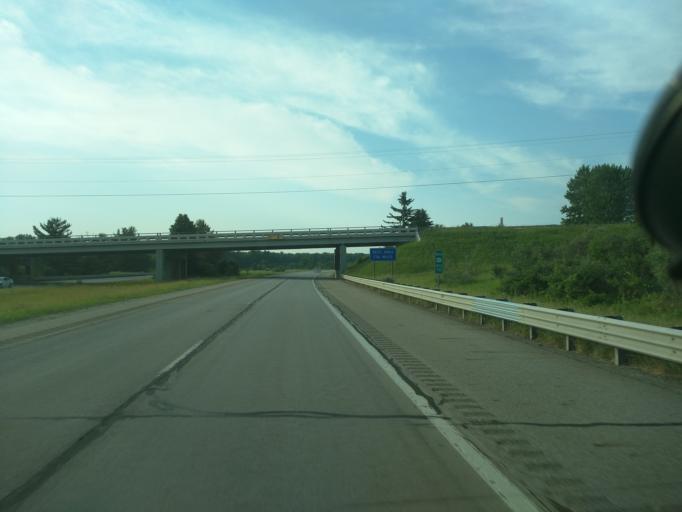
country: US
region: Michigan
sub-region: Ingham County
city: Holt
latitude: 42.6394
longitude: -84.4783
